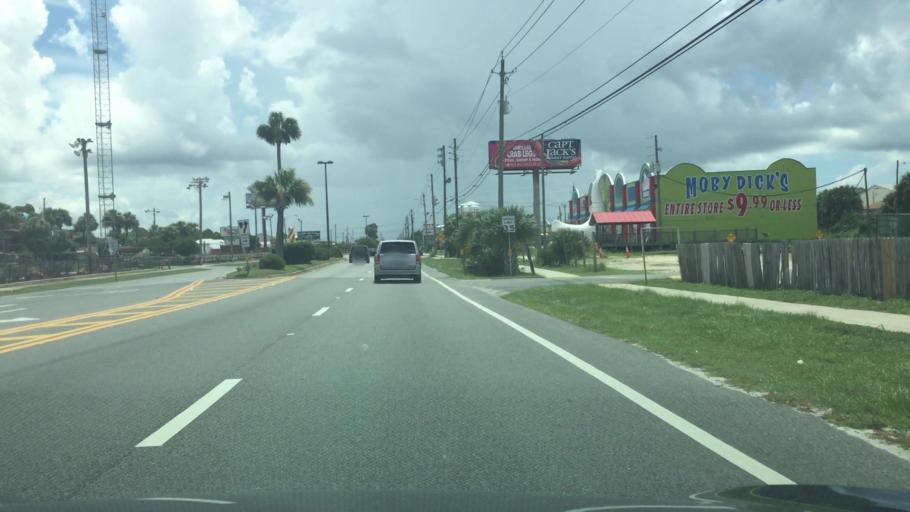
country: US
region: Florida
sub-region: Bay County
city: Panama City Beach
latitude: 30.1673
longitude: -85.7887
